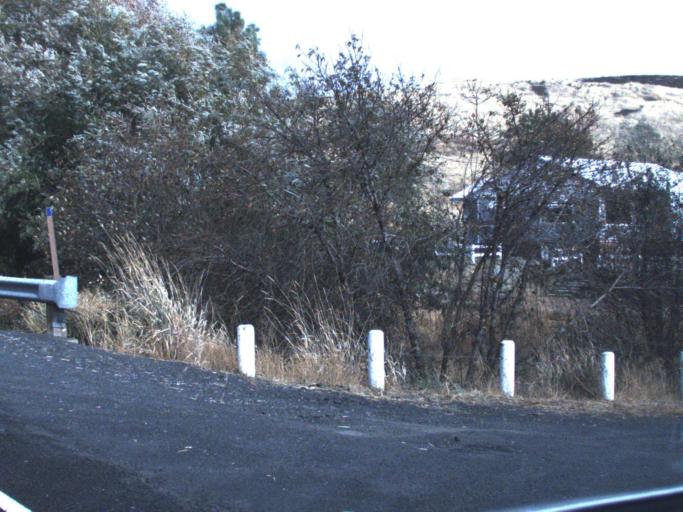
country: US
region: Washington
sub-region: Okanogan County
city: Coulee Dam
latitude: 47.8481
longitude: -118.7172
